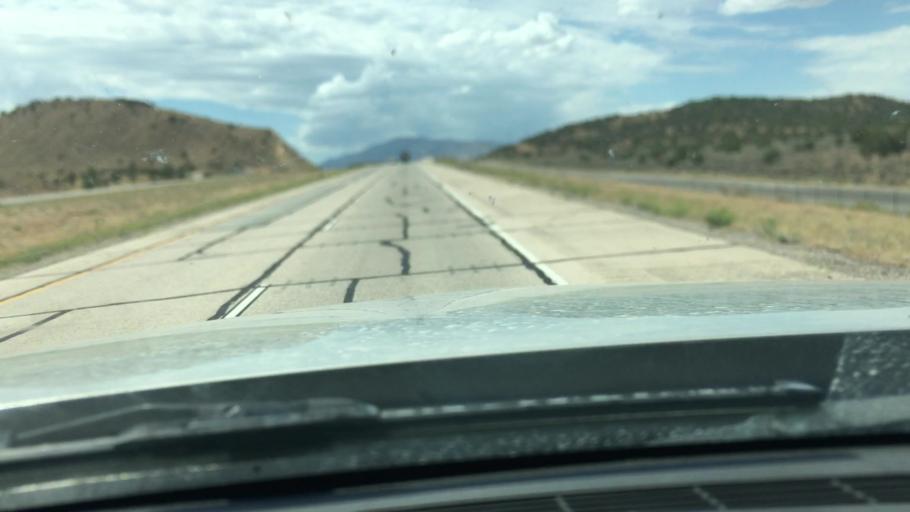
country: US
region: Utah
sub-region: Sanpete County
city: Gunnison
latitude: 39.3343
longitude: -112.0817
